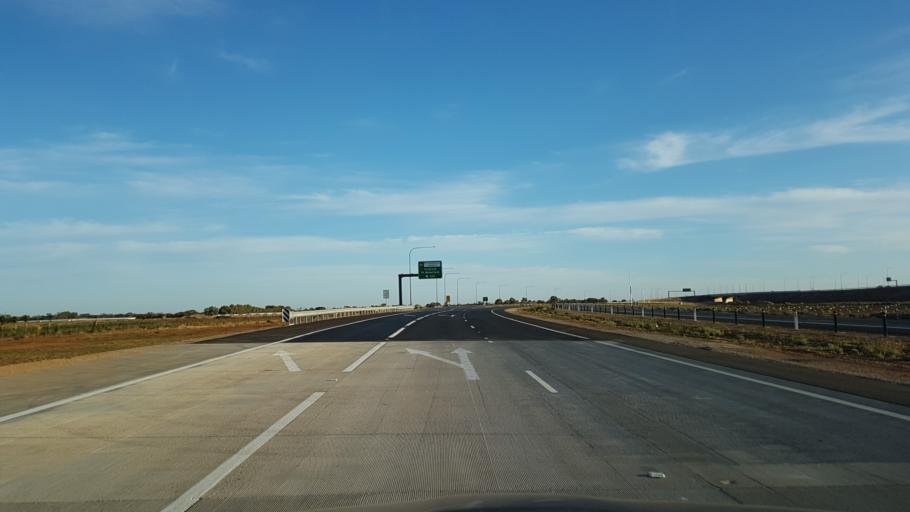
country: AU
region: South Australia
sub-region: Playford
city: Virginia
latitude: -34.7126
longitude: 138.5712
